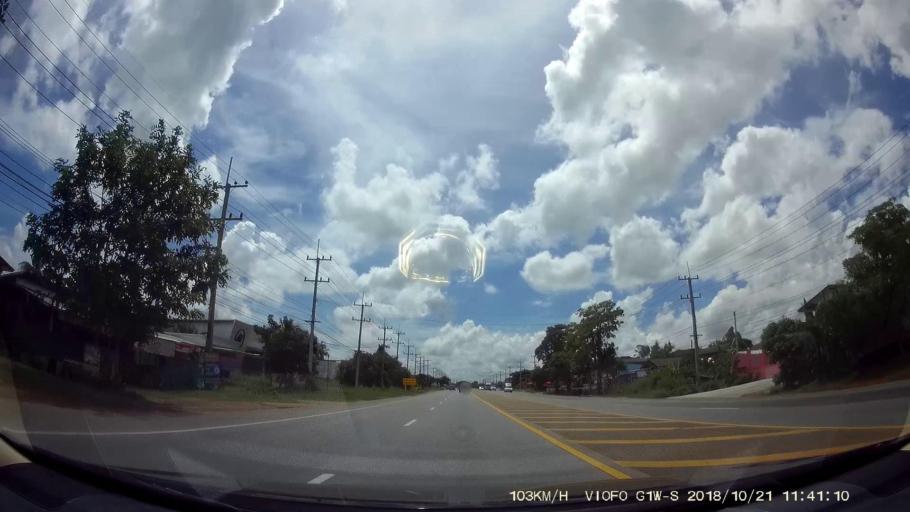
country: TH
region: Chaiyaphum
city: Chaiyaphum
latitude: 15.7029
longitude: 102.0149
